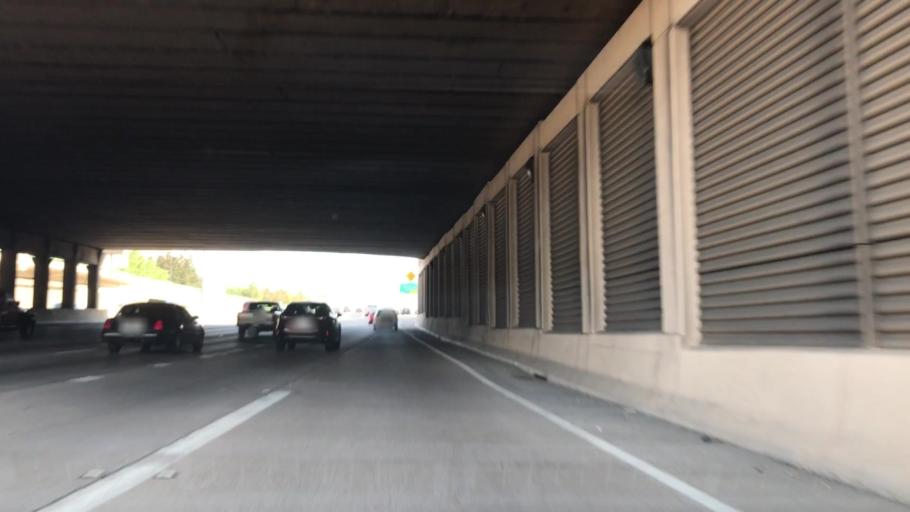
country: US
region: Texas
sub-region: Dallas County
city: University Park
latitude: 32.8716
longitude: -96.7699
